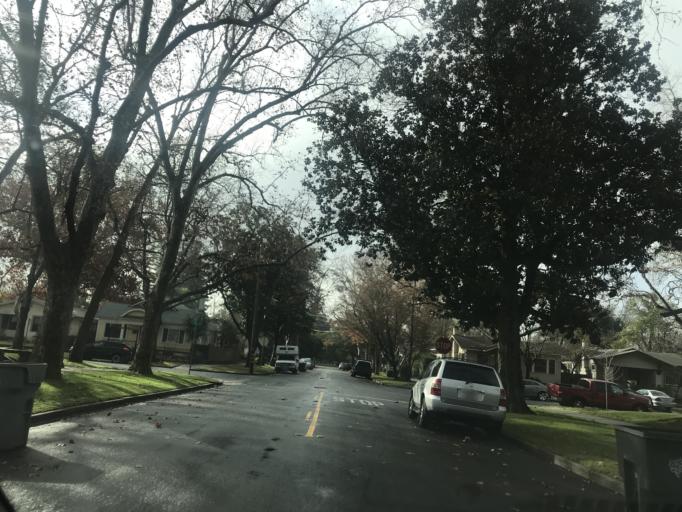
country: US
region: California
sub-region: Sacramento County
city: Sacramento
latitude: 38.5792
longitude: -121.4604
